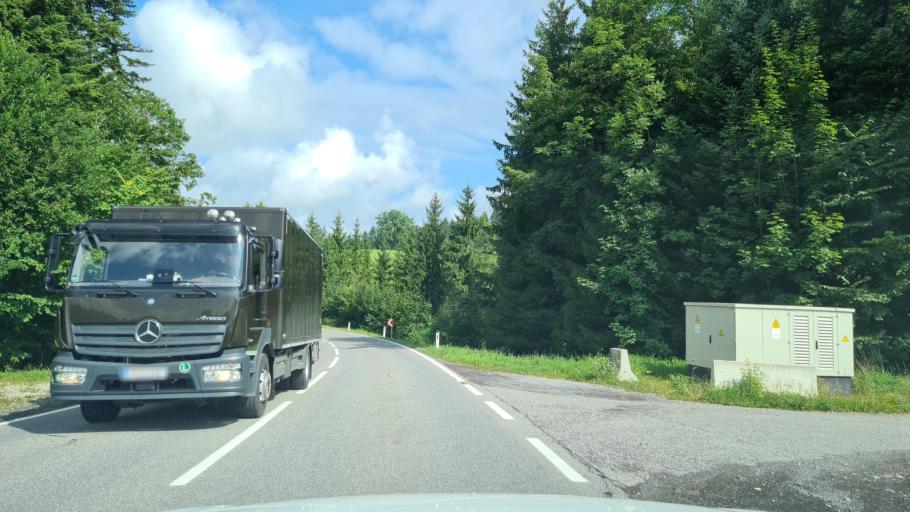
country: AT
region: Vorarlberg
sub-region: Politischer Bezirk Bregenz
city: Egg
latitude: 47.4499
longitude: 9.8971
